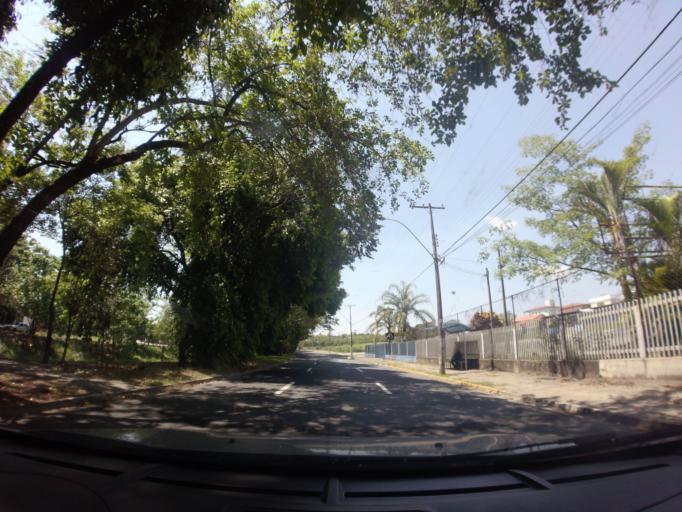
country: BR
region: Sao Paulo
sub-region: Piracicaba
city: Piracicaba
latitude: -22.7242
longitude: -47.6252
